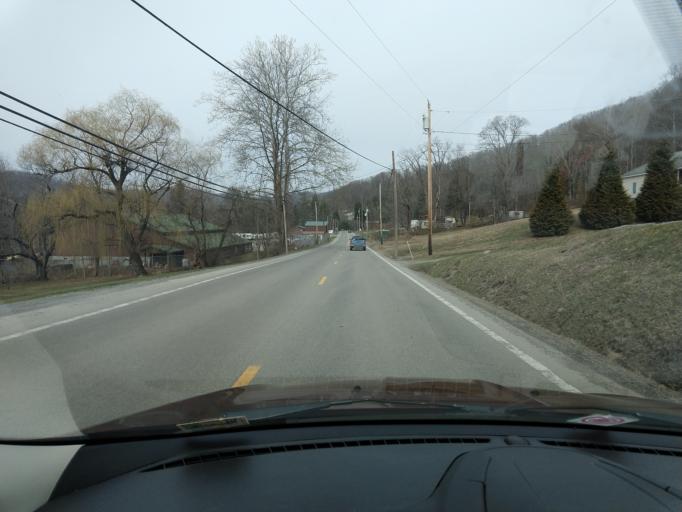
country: US
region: West Virginia
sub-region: Tucker County
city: Parsons
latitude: 39.0930
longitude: -79.6592
